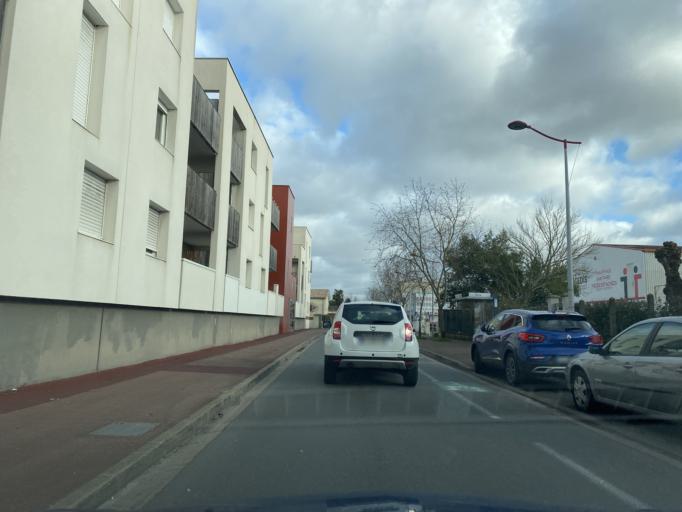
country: FR
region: Aquitaine
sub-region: Departement de la Gironde
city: Le Haillan
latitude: 44.8415
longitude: -0.6698
